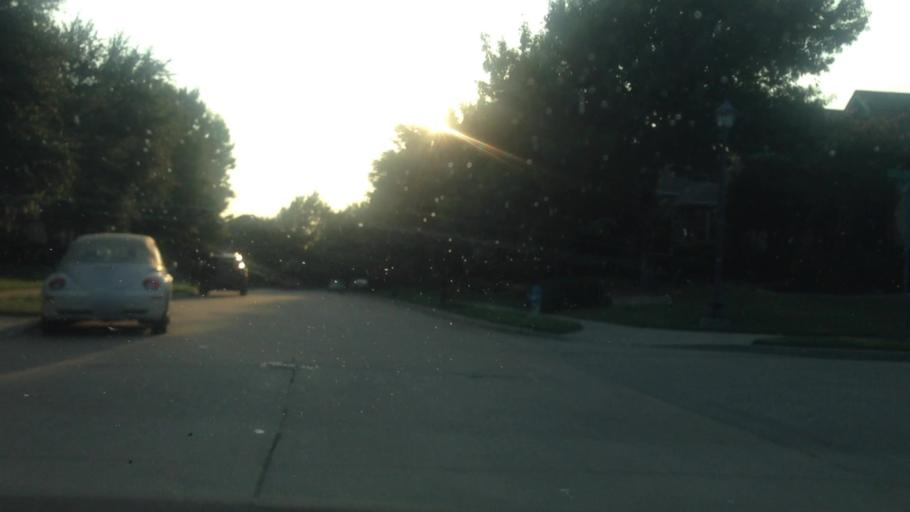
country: US
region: Texas
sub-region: Denton County
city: The Colony
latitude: 33.1245
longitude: -96.8720
